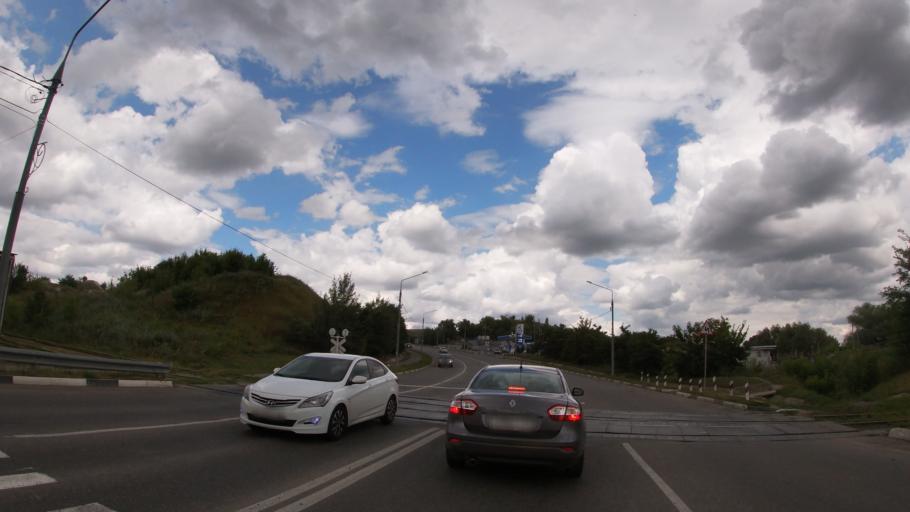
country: RU
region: Belgorod
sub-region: Belgorodskiy Rayon
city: Belgorod
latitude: 50.6087
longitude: 36.6132
